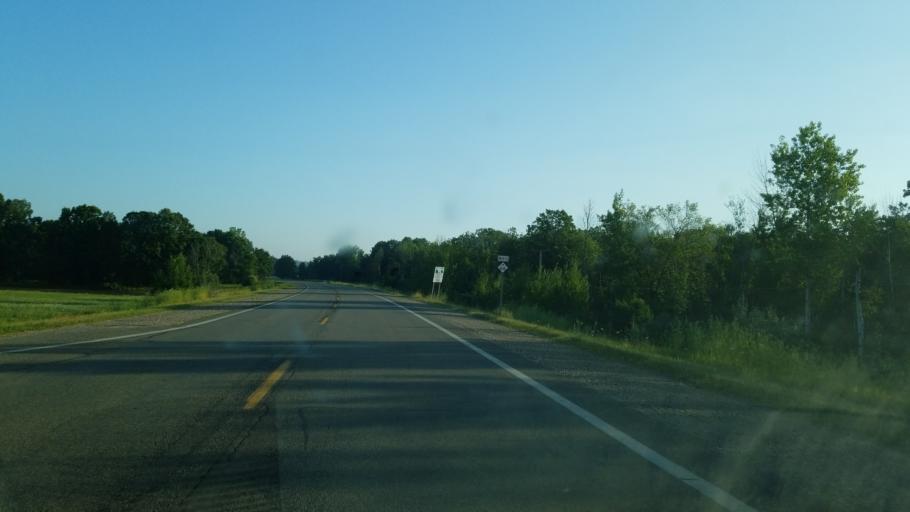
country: US
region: Michigan
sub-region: Montcalm County
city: Stanton
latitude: 43.3216
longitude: -85.0847
